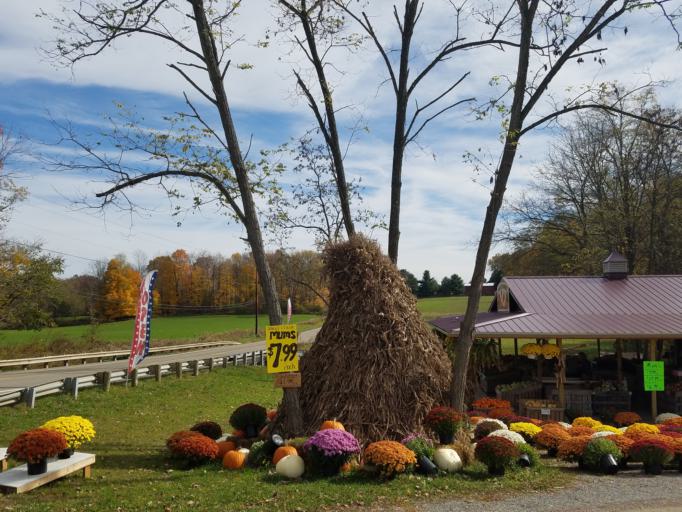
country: US
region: Ohio
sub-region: Wayne County
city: Shreve
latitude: 40.5892
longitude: -82.0760
